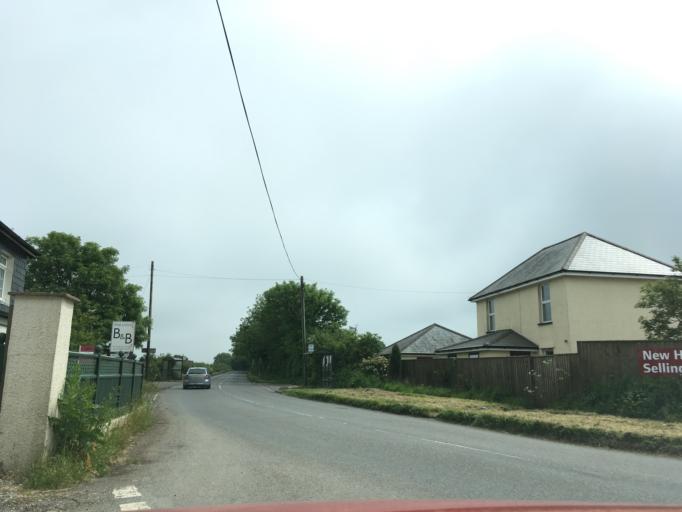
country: GB
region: England
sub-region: Devon
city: Totnes
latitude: 50.3630
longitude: -3.6770
